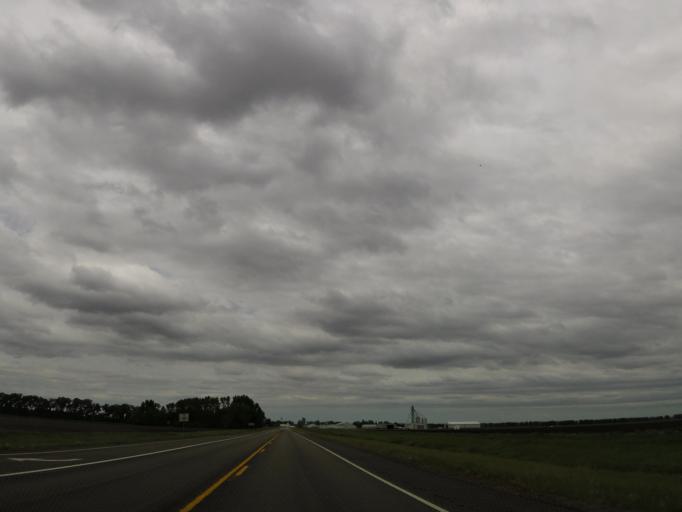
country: US
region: North Dakota
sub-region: Walsh County
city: Grafton
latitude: 48.6015
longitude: -97.4476
